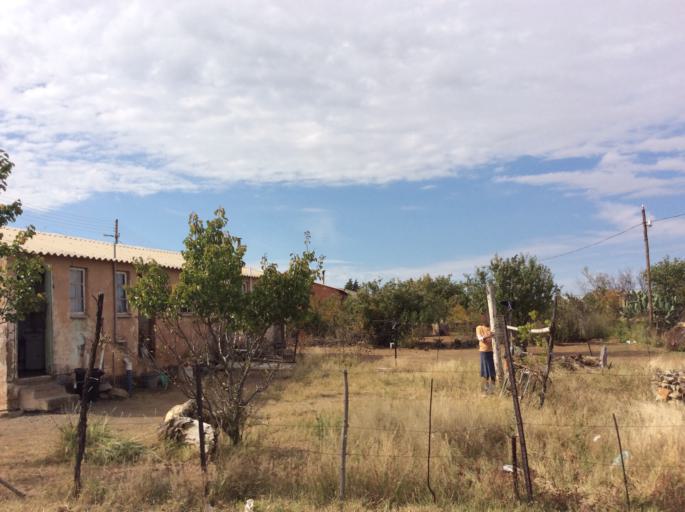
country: LS
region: Mafeteng
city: Mafeteng
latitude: -29.7231
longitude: 27.0084
